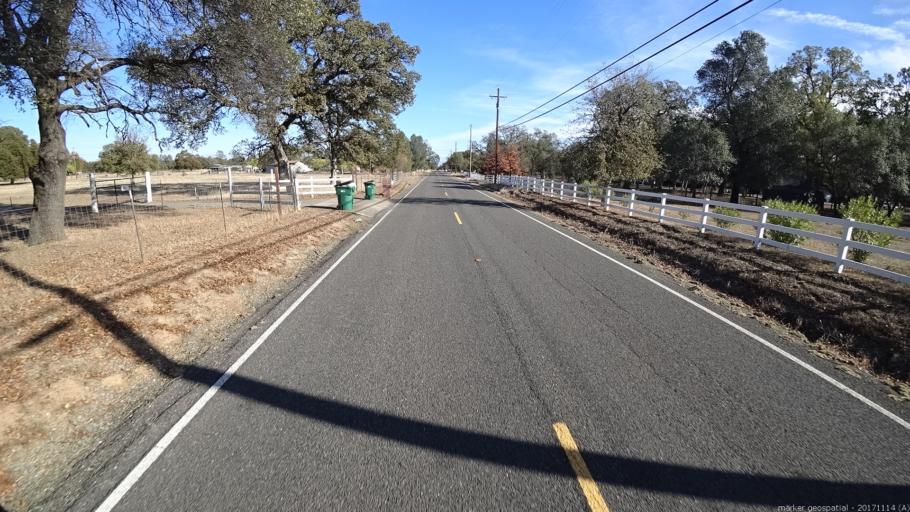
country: US
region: California
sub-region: Shasta County
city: Anderson
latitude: 40.3884
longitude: -122.4405
